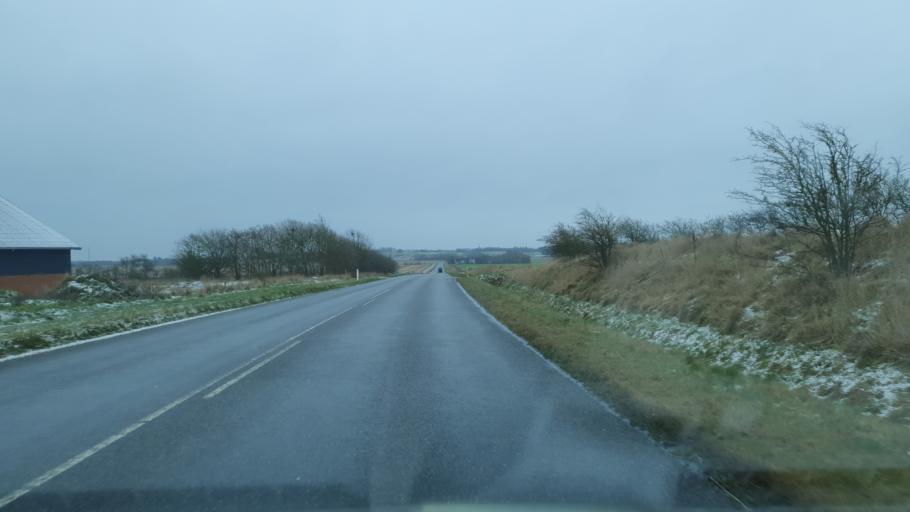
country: DK
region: North Denmark
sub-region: Jammerbugt Kommune
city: Brovst
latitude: 57.1240
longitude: 9.4897
